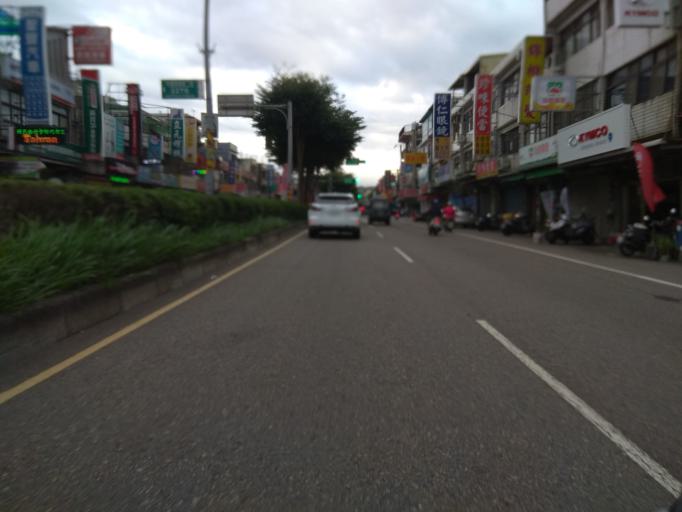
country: TW
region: Taiwan
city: Daxi
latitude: 24.9128
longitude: 121.2106
